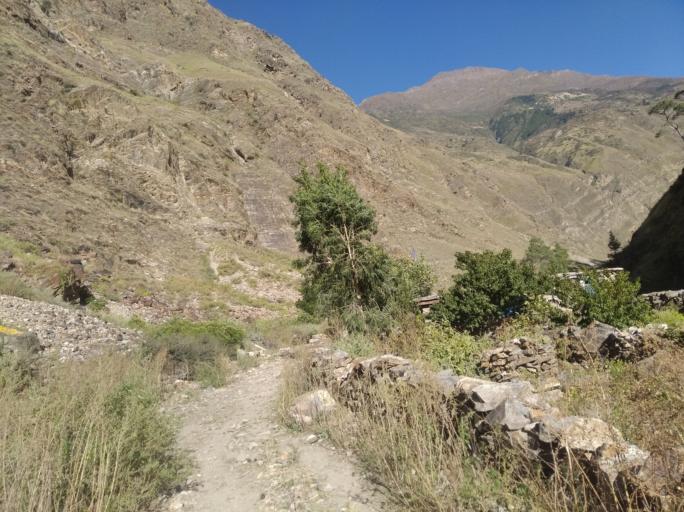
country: NP
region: Western Region
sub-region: Dhawalagiri Zone
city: Jomsom
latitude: 28.9400
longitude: 82.9437
